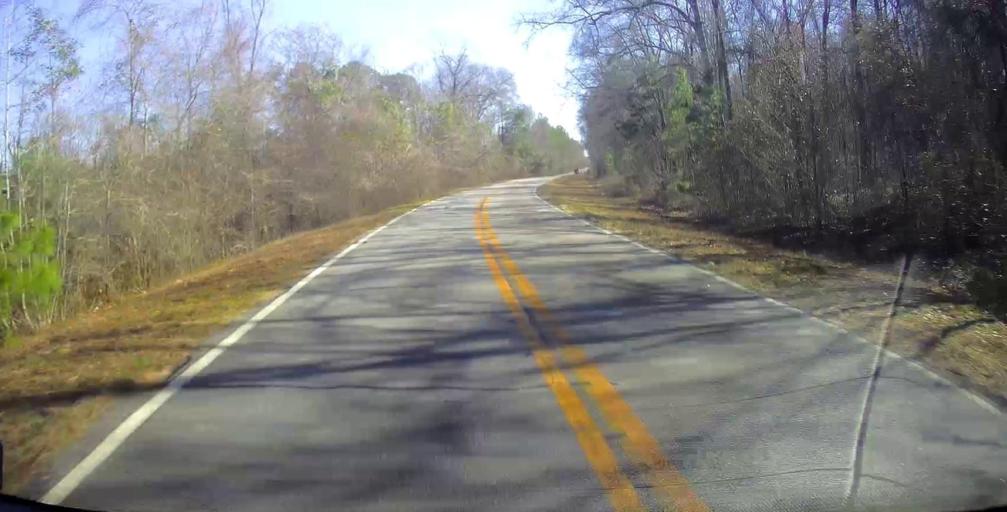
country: US
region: Georgia
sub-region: Peach County
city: Byron
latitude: 32.6083
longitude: -83.8031
